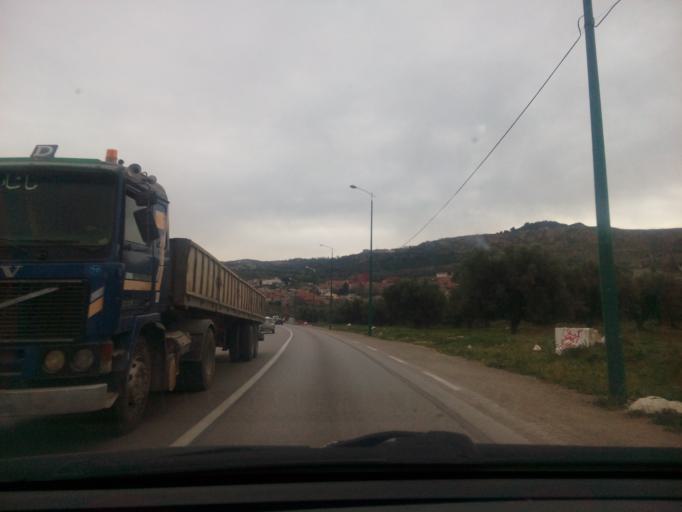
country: DZ
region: Tlemcen
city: Mansoura
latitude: 34.8651
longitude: -1.3469
